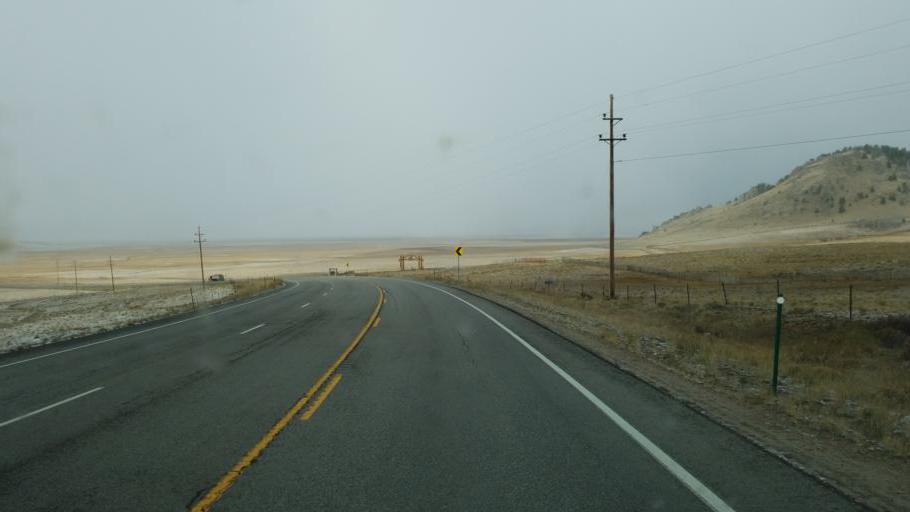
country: US
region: Colorado
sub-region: Summit County
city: Breckenridge
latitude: 39.4065
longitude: -105.7737
